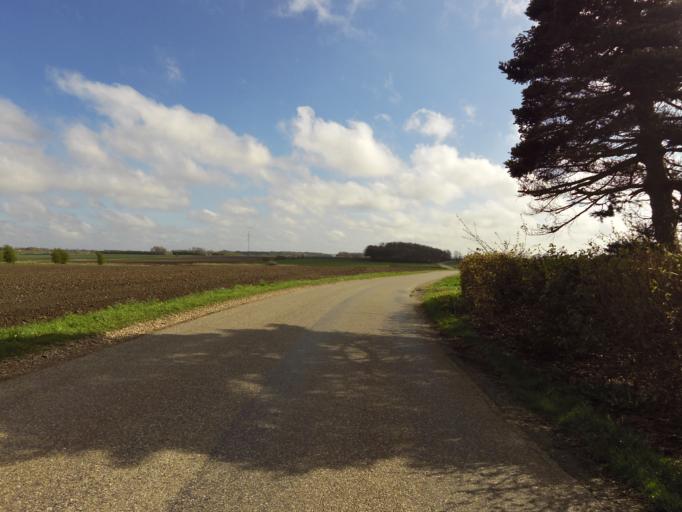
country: DK
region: South Denmark
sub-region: Vejen Kommune
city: Rodding
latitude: 55.3486
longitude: 8.9909
